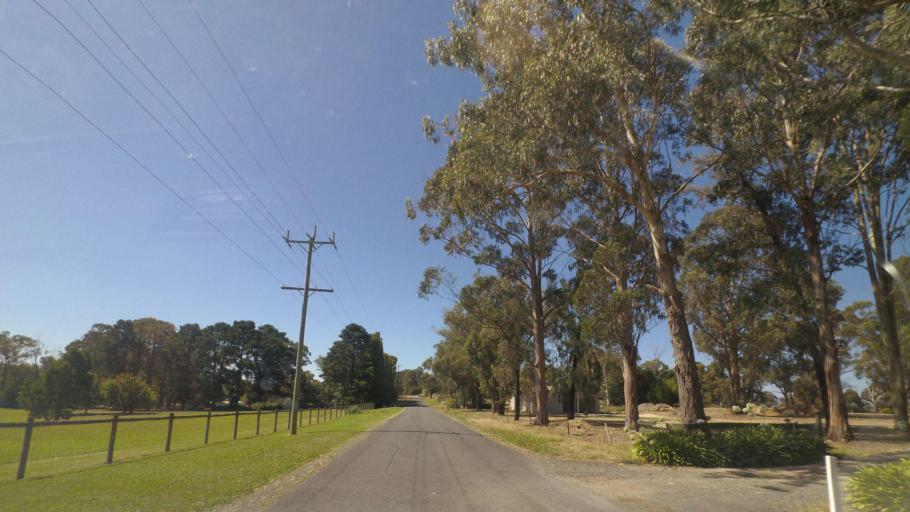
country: AU
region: Victoria
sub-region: Yarra Ranges
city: Lilydale
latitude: -37.7443
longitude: 145.3336
